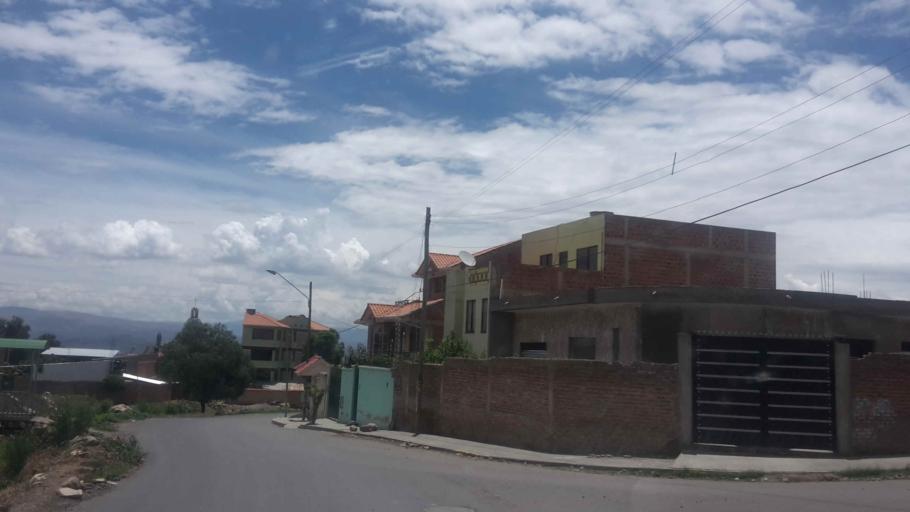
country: BO
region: Cochabamba
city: Cochabamba
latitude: -17.3470
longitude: -66.1797
